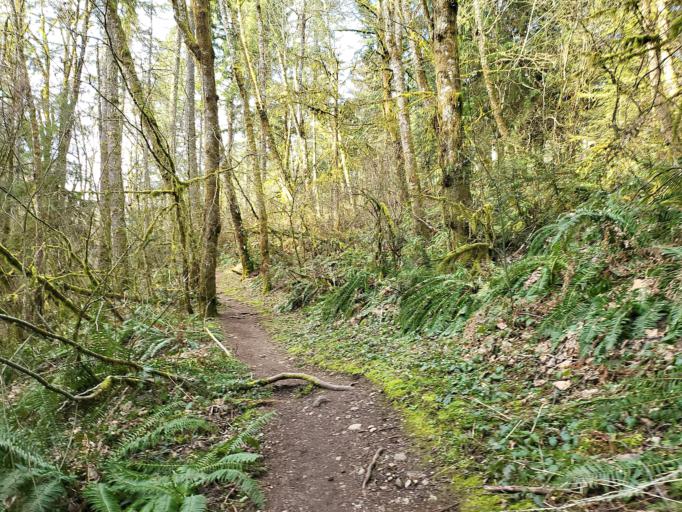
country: US
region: Washington
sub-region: King County
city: East Renton Highlands
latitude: 47.5139
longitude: -122.1215
